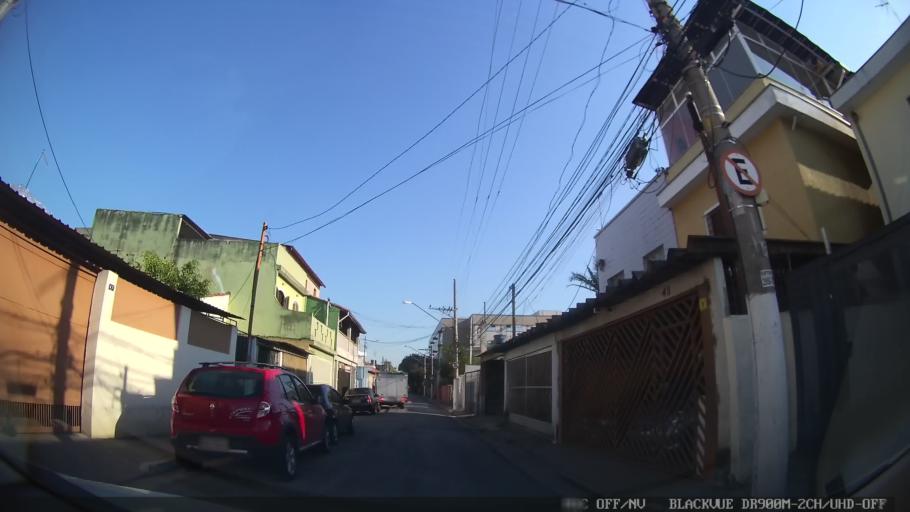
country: BR
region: Sao Paulo
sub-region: Sao Paulo
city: Sao Paulo
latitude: -23.5071
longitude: -46.6690
